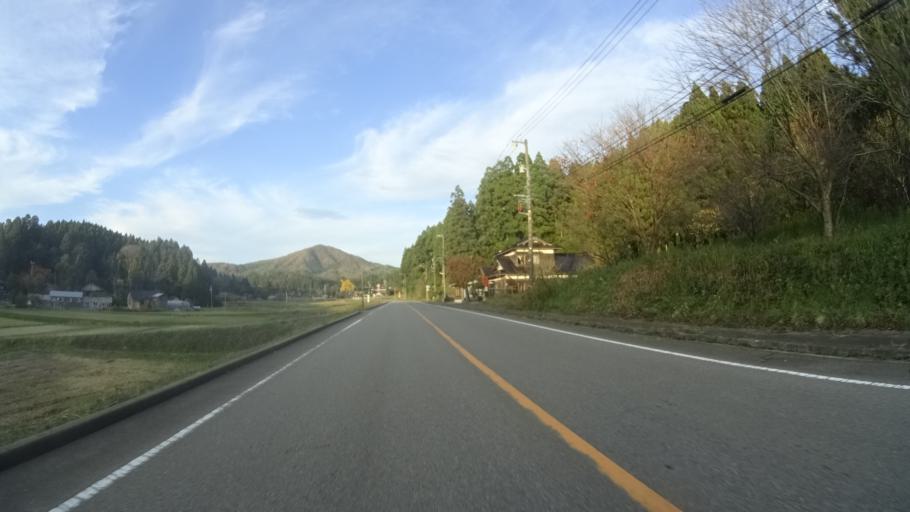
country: JP
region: Ishikawa
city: Nanao
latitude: 37.1863
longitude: 136.7148
